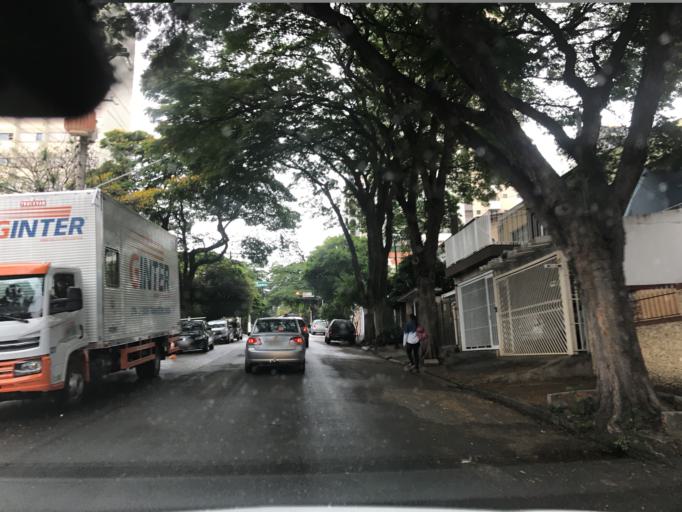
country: BR
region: Sao Paulo
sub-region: Sao Paulo
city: Sao Paulo
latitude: -23.5367
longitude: -46.6756
